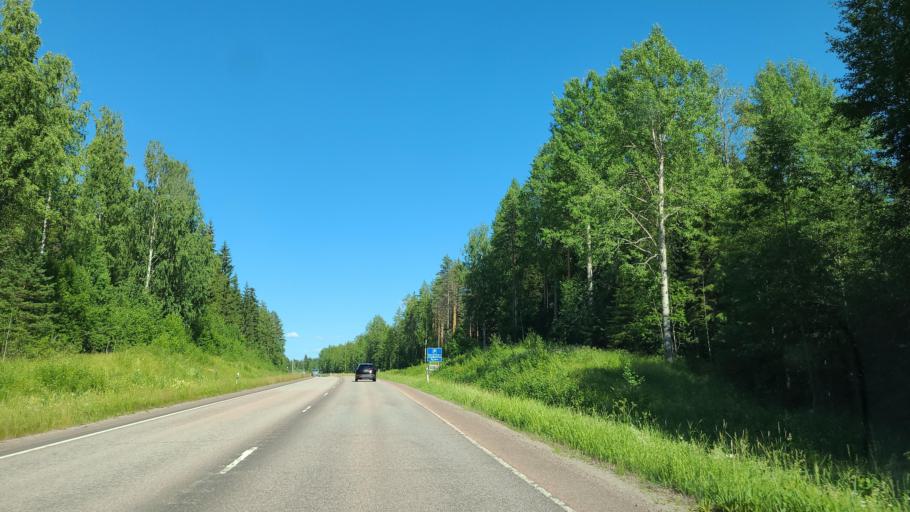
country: FI
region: Central Finland
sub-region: Jyvaeskylae
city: Petaejaevesi
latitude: 62.2692
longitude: 25.2994
